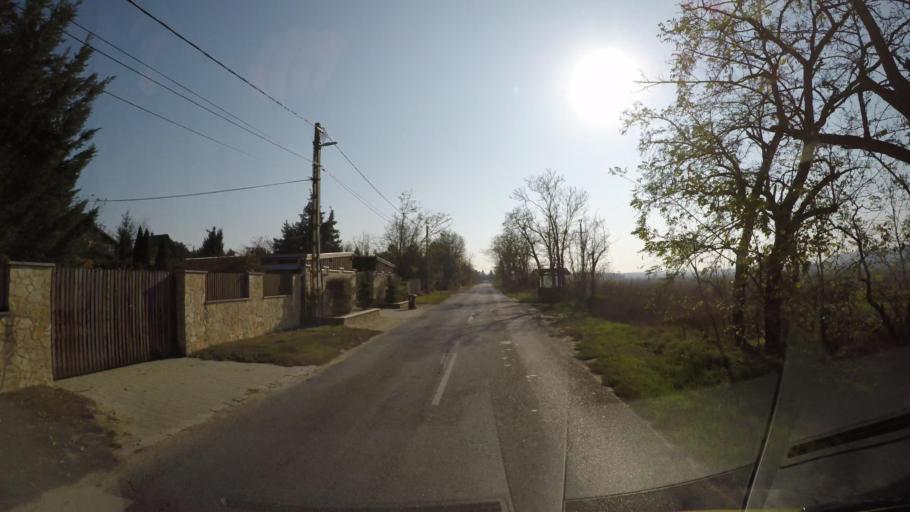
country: HU
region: Pest
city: Leanyfalu
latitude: 47.7091
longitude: 19.1068
